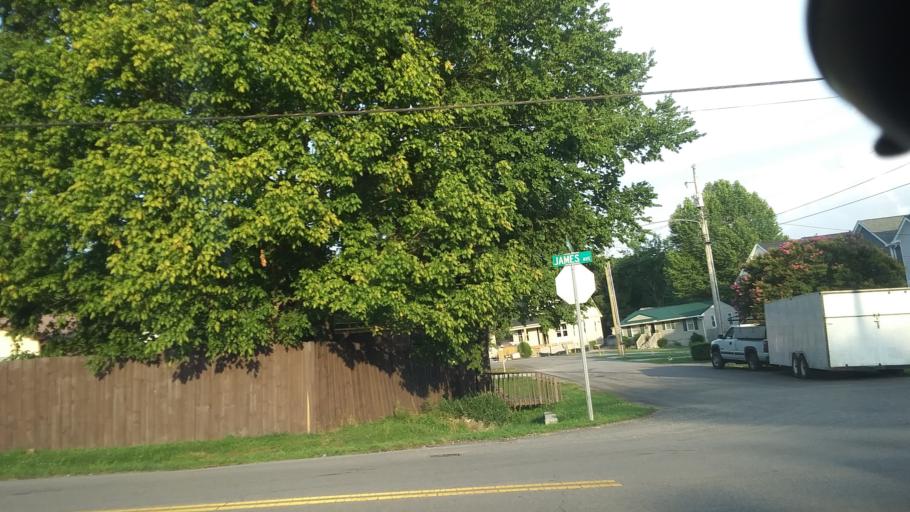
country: US
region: Tennessee
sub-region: Davidson County
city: Belle Meade
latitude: 36.1591
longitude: -86.8764
